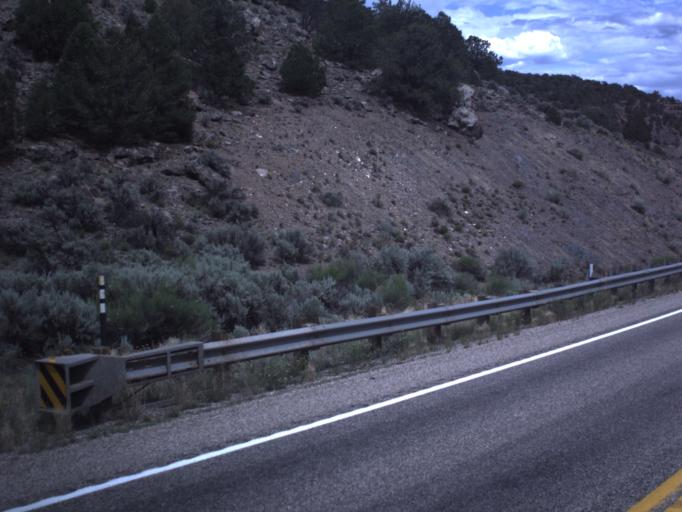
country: US
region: Utah
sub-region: Garfield County
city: Panguitch
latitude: 37.9683
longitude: -112.4766
